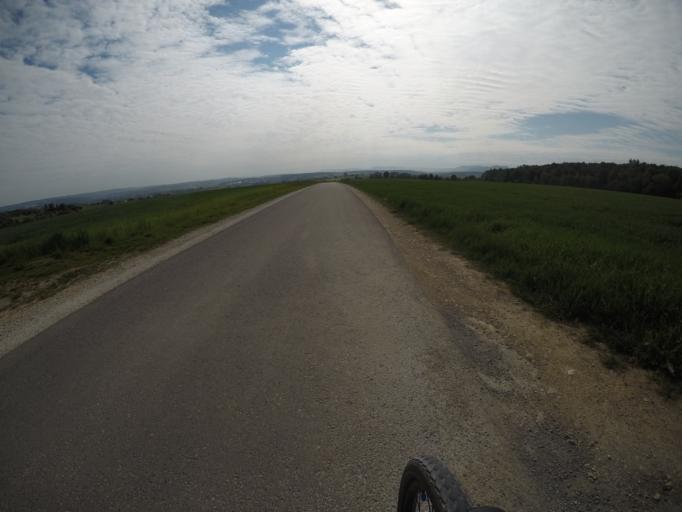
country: DE
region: Baden-Wuerttemberg
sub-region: Regierungsbezirk Stuttgart
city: Unterensingen
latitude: 48.6597
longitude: 9.3302
